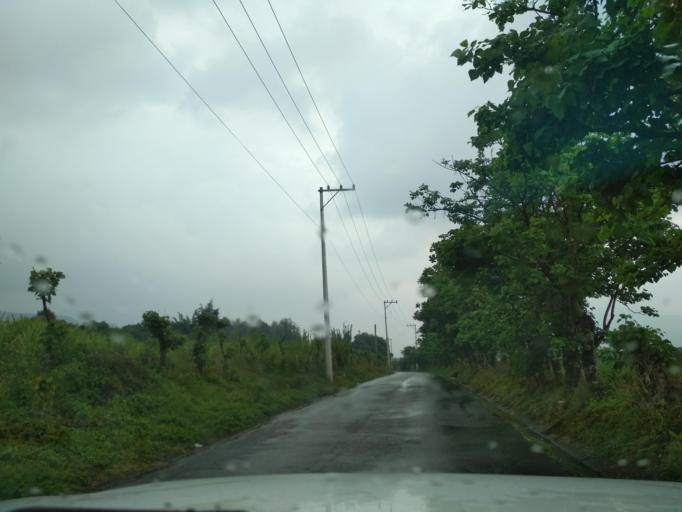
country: MX
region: Veracruz
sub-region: Mariano Escobedo
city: Mariano Escobedo
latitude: 18.9045
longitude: -97.1247
